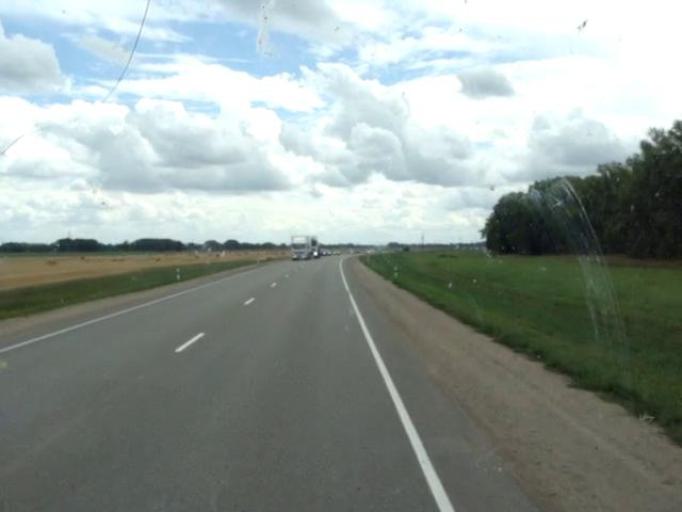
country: RU
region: Altai Krai
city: Shubenka
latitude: 52.6847
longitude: 85.0428
